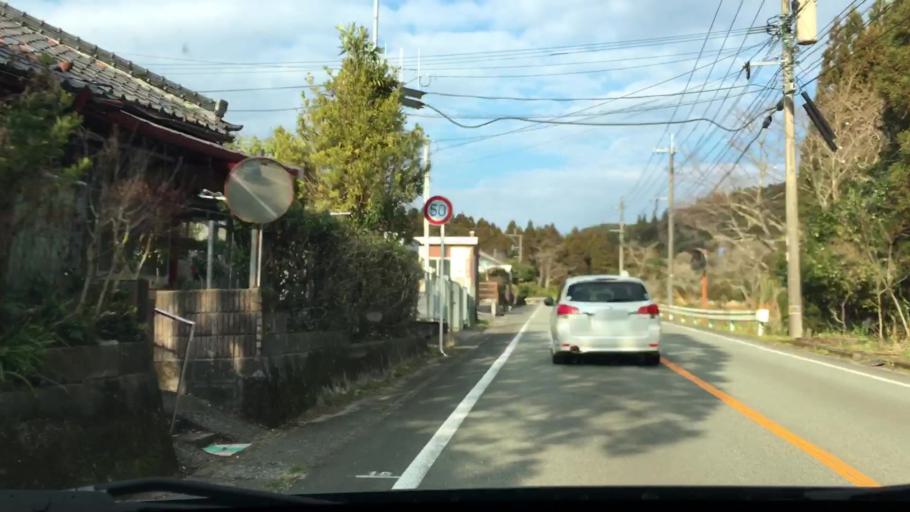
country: JP
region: Miyazaki
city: Nichinan
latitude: 31.7245
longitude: 131.3300
